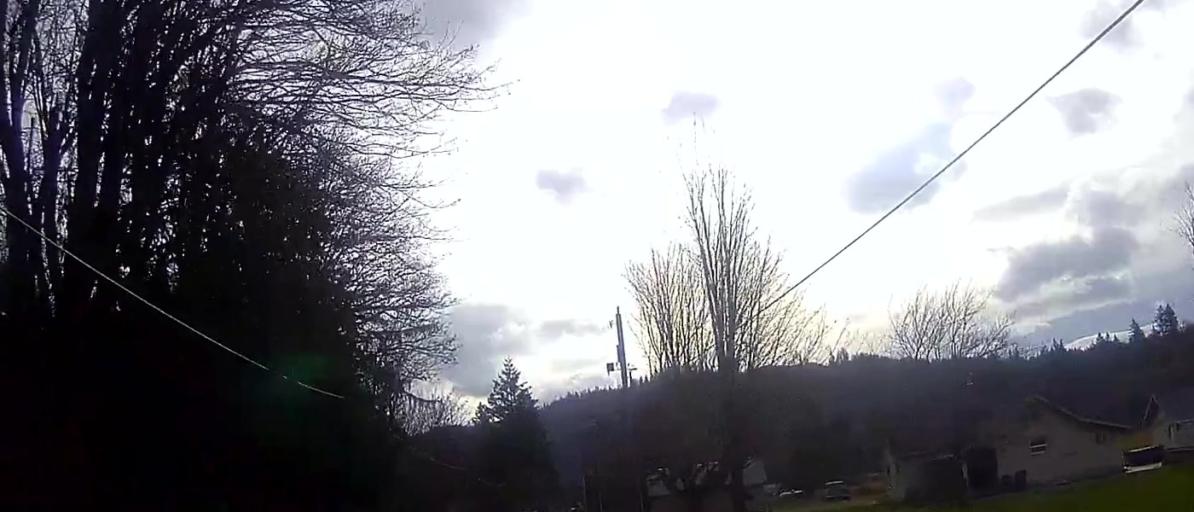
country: US
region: Washington
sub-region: Skagit County
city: Sedro-Woolley
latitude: 48.5685
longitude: -122.2981
